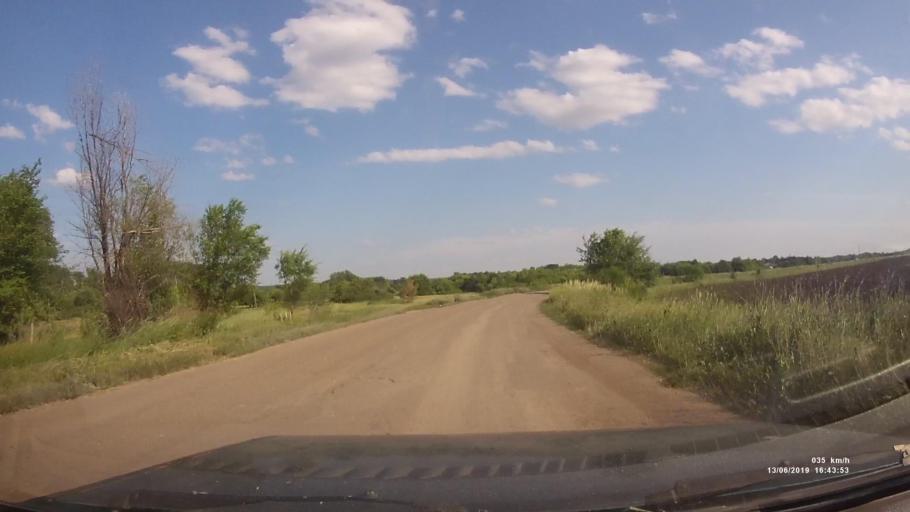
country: RU
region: Rostov
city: Kazanskaya
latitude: 49.9482
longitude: 41.4221
